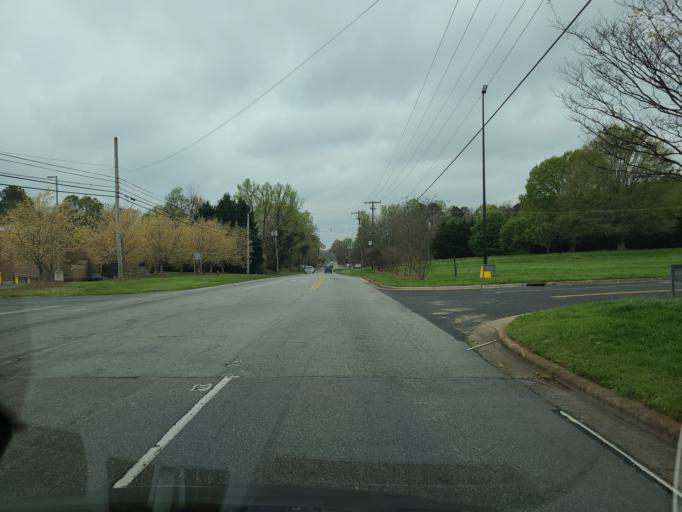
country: US
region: North Carolina
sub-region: Lincoln County
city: Lincolnton
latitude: 35.4939
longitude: -81.2472
